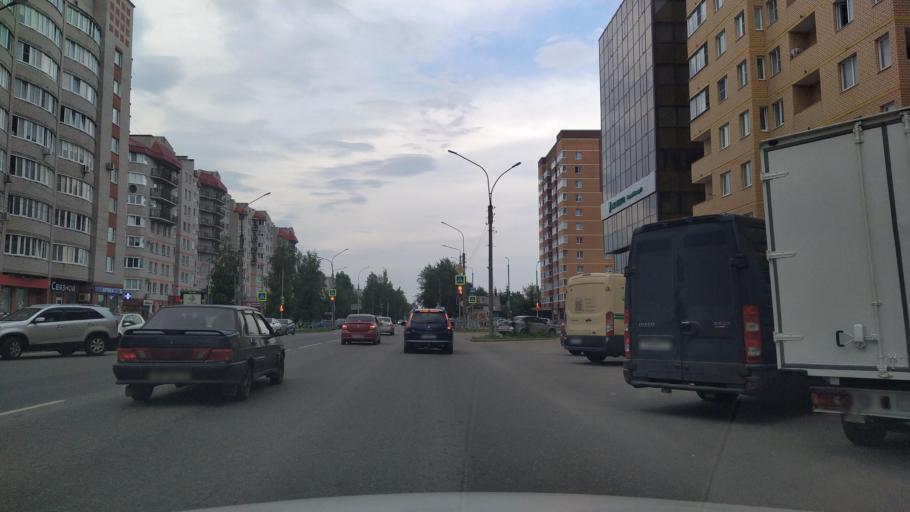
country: RU
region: Novgorod
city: Velikiy Novgorod
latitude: 58.5158
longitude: 31.2456
